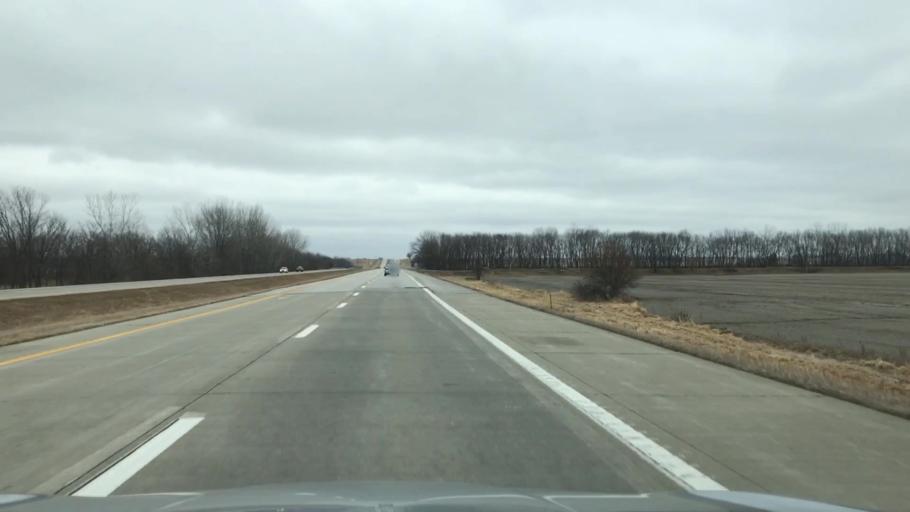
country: US
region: Missouri
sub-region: Livingston County
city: Chillicothe
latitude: 39.7768
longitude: -93.4210
